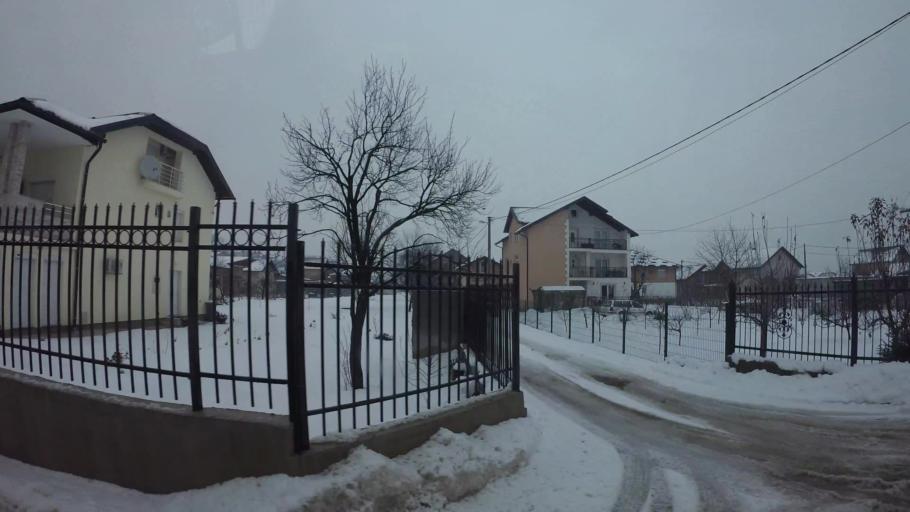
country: BA
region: Federation of Bosnia and Herzegovina
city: Hadzici
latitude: 43.8409
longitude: 18.2708
